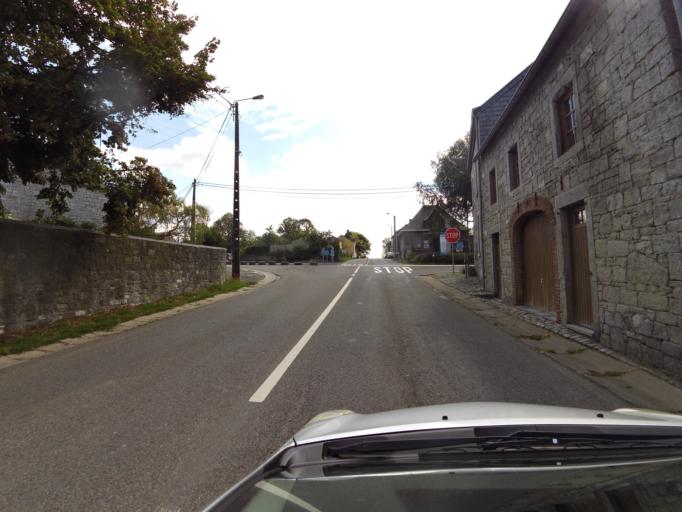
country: BE
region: Wallonia
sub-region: Province de Namur
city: Somme-Leuze
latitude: 50.3551
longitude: 5.3125
